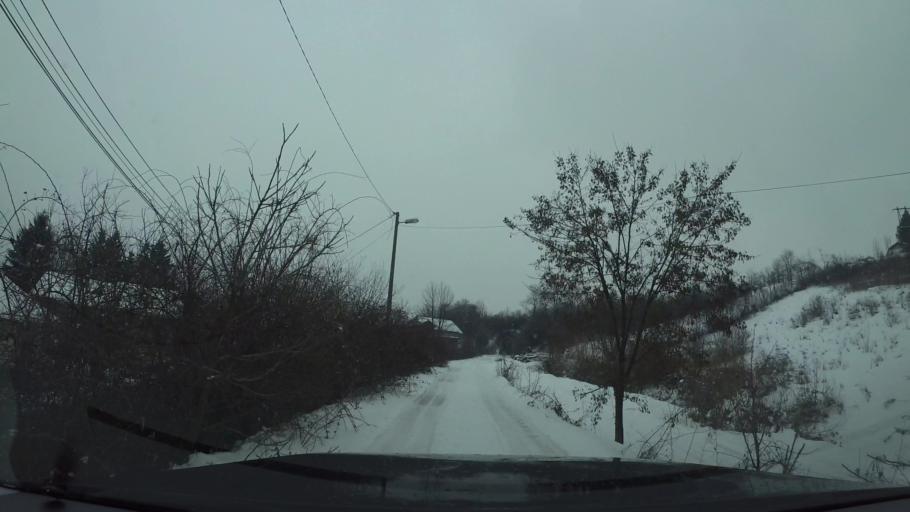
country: BA
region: Federation of Bosnia and Herzegovina
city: Hadzici
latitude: 43.8511
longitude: 18.2770
